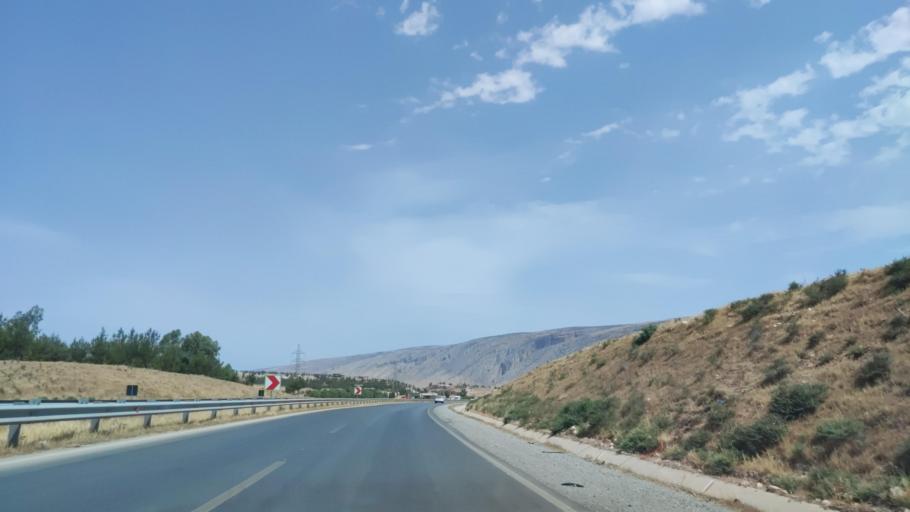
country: IQ
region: Arbil
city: Shaqlawah
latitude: 36.4769
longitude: 44.3806
